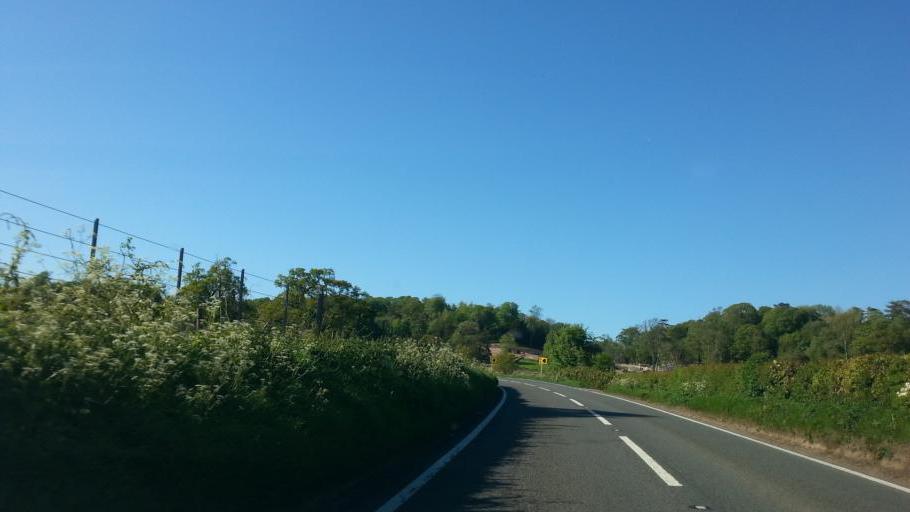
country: GB
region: England
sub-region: Somerset
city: Castle Cary
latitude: 51.0731
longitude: -2.4851
